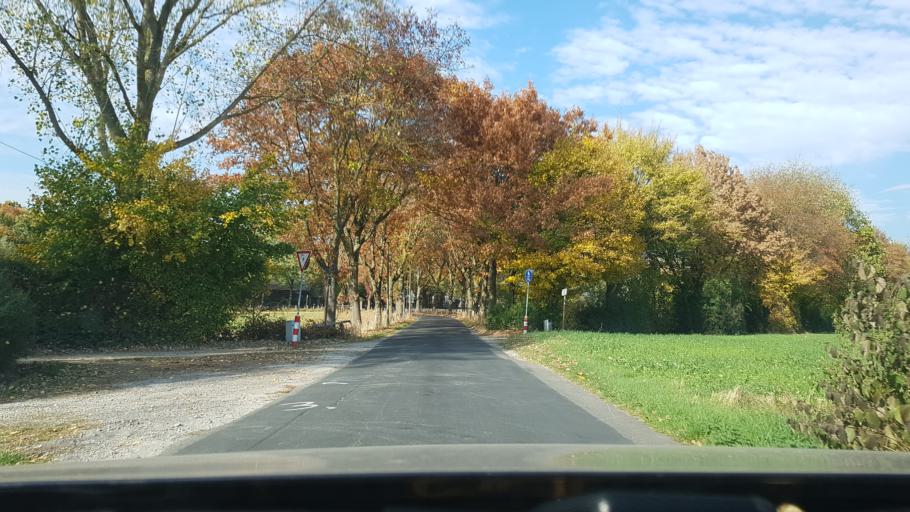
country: DE
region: North Rhine-Westphalia
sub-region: Regierungsbezirk Dusseldorf
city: Moers
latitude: 51.4275
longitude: 6.6191
